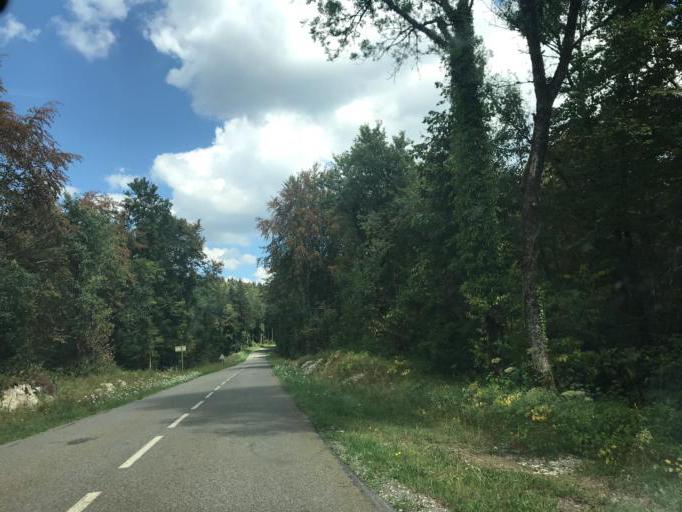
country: FR
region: Franche-Comte
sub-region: Departement du Jura
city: Clairvaux-les-Lacs
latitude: 46.5125
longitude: 5.7883
